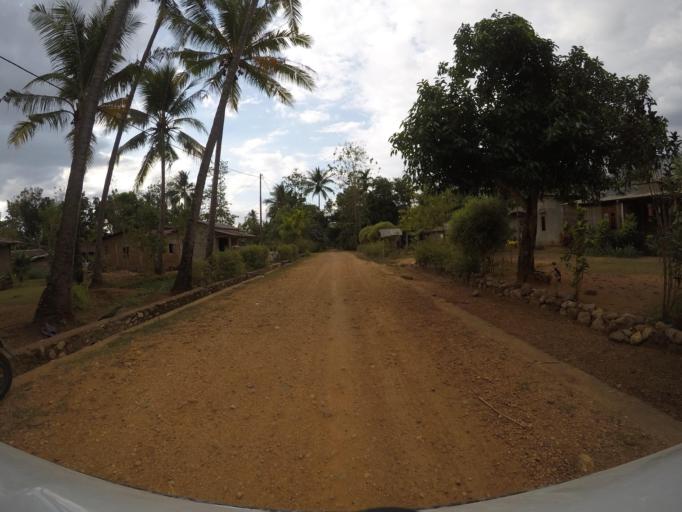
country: TL
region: Bobonaro
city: Maliana
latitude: -8.9635
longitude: 125.2177
